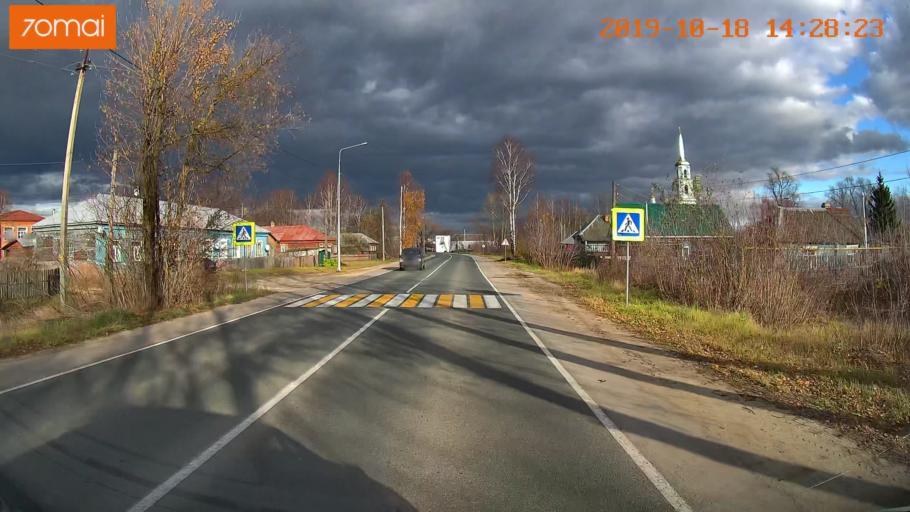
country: RU
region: Rjazan
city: Tuma
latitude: 55.1484
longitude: 40.5516
